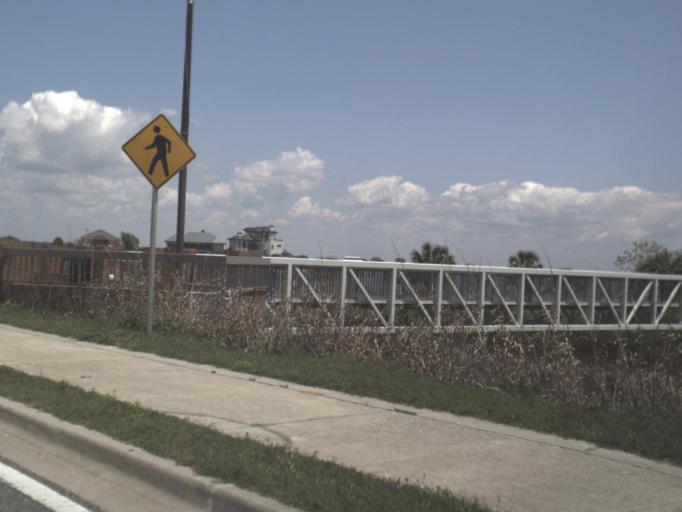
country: US
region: Florida
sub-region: Escambia County
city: Pensacola
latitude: 30.4120
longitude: -87.2029
